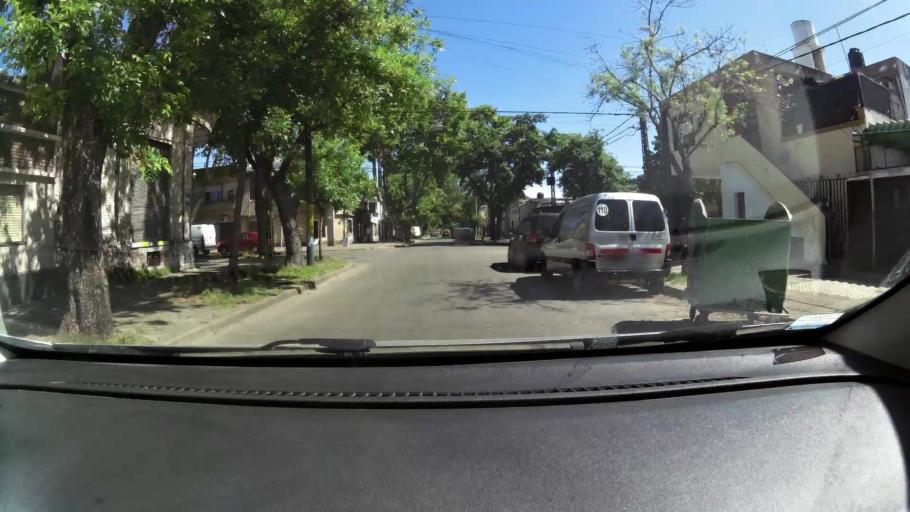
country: AR
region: Santa Fe
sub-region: Departamento de Rosario
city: Rosario
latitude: -32.9459
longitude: -60.6837
